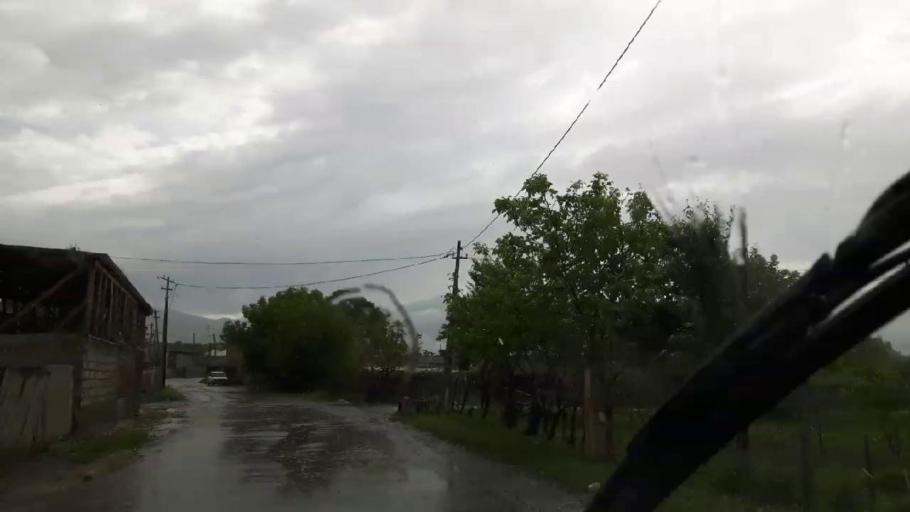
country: GE
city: Agara
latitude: 42.0092
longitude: 43.7646
